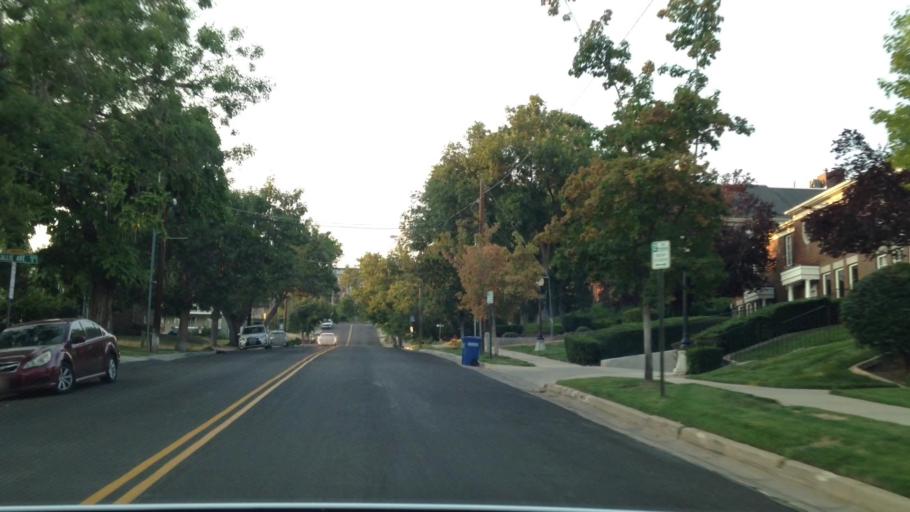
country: US
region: Utah
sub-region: Salt Lake County
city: Salt Lake City
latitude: 40.7798
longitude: -111.8775
